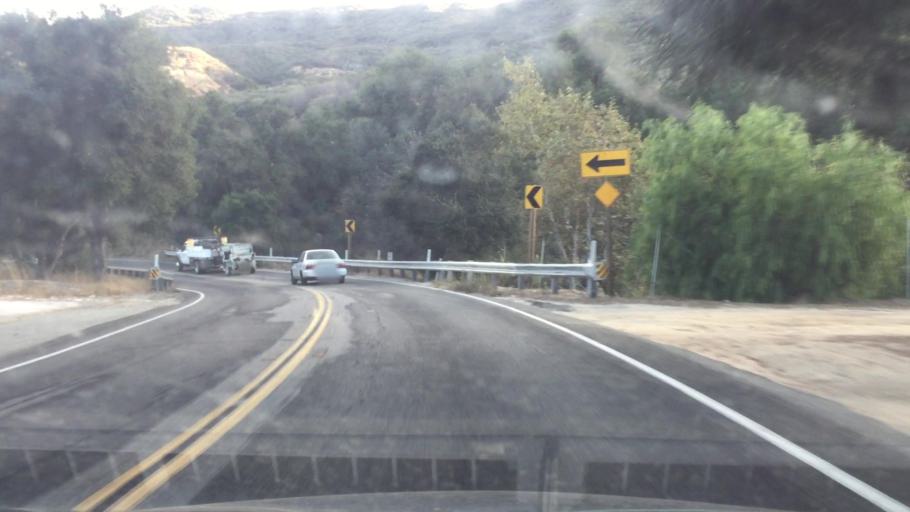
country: US
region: California
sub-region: Riverside County
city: Lakeland Village
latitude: 33.6517
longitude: -117.3956
